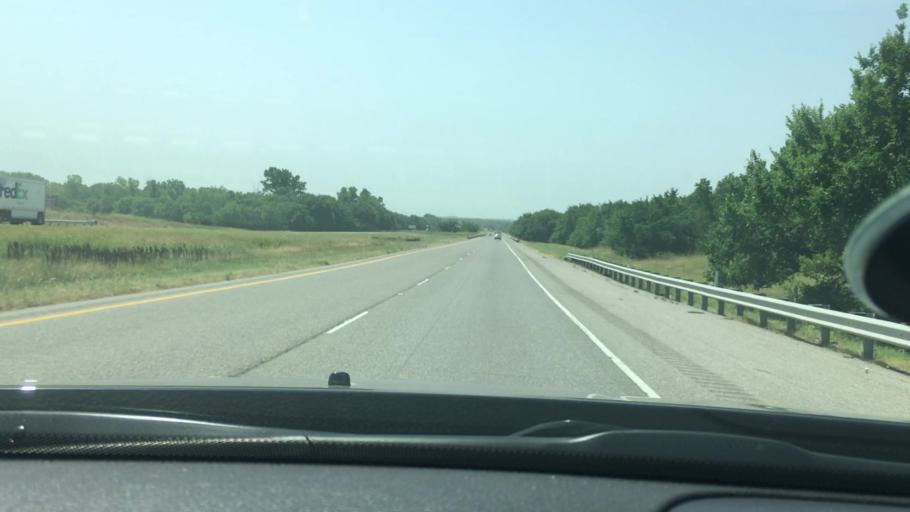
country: US
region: Oklahoma
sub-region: Murray County
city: Davis
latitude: 34.5371
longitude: -97.1886
